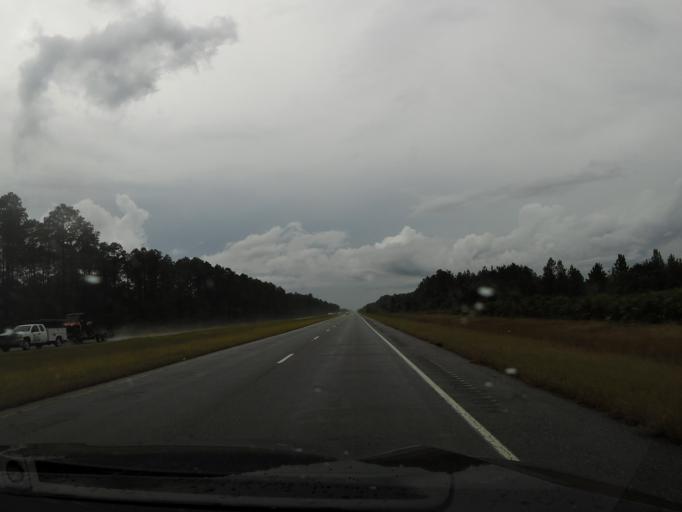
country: US
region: Georgia
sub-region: Wayne County
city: Jesup
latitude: 31.4775
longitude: -81.7287
